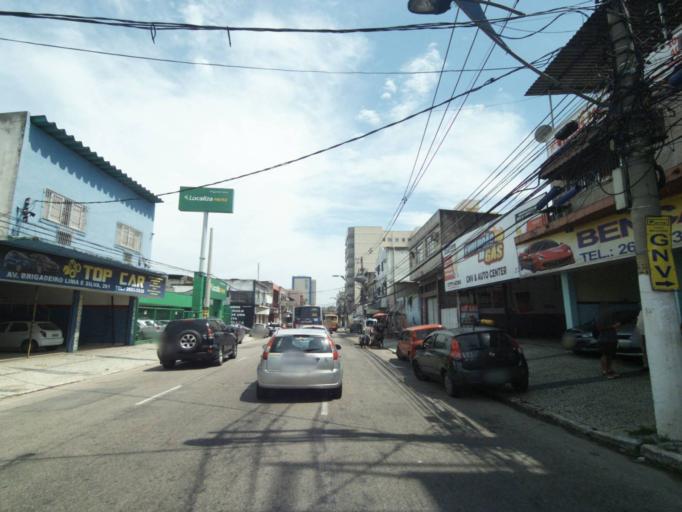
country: BR
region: Rio de Janeiro
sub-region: Duque De Caxias
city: Duque de Caxias
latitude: -22.7996
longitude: -43.2930
